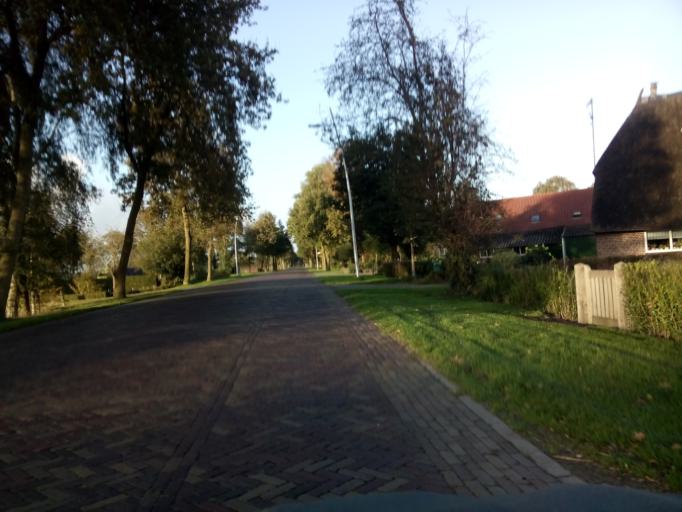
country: NL
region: Overijssel
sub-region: Gemeente Staphorst
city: Staphorst
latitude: 52.5966
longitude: 6.1947
